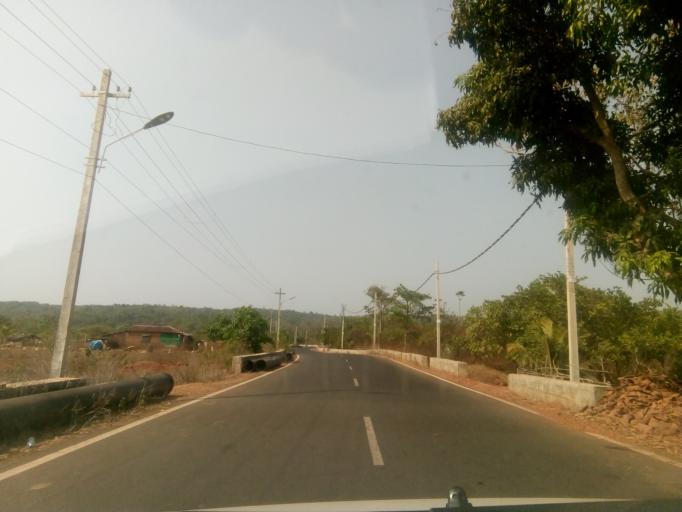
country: IN
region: Goa
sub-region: North Goa
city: Pernem
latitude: 15.7133
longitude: 73.8543
